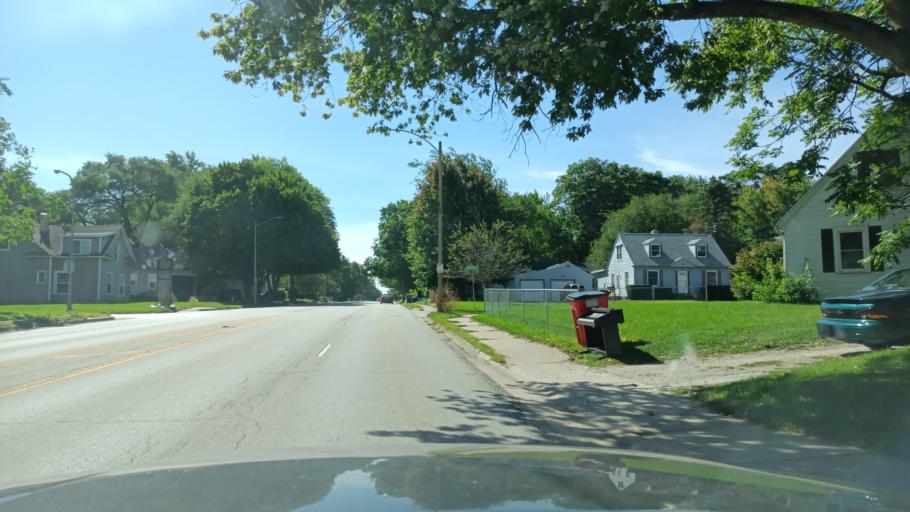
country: US
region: Illinois
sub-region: Champaign County
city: Champaign
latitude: 40.1302
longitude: -88.2437
